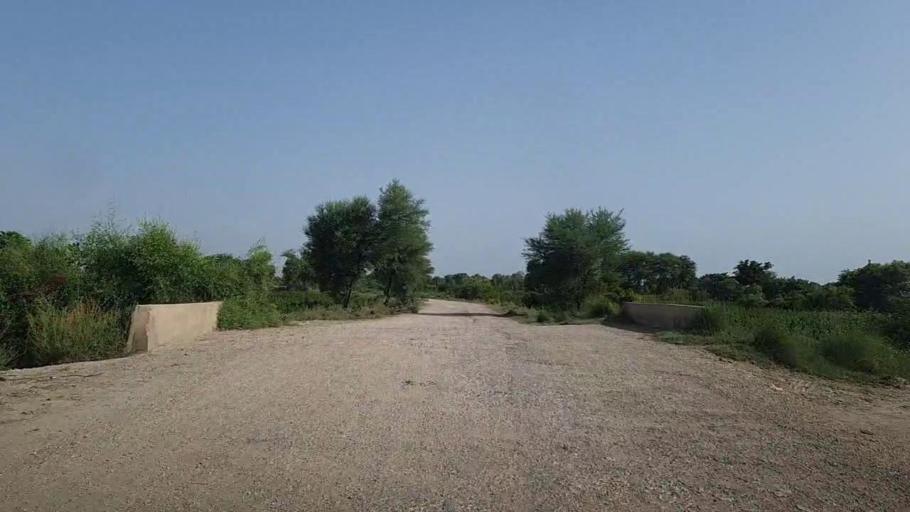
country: PK
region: Sindh
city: Karaundi
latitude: 26.8704
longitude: 68.3291
